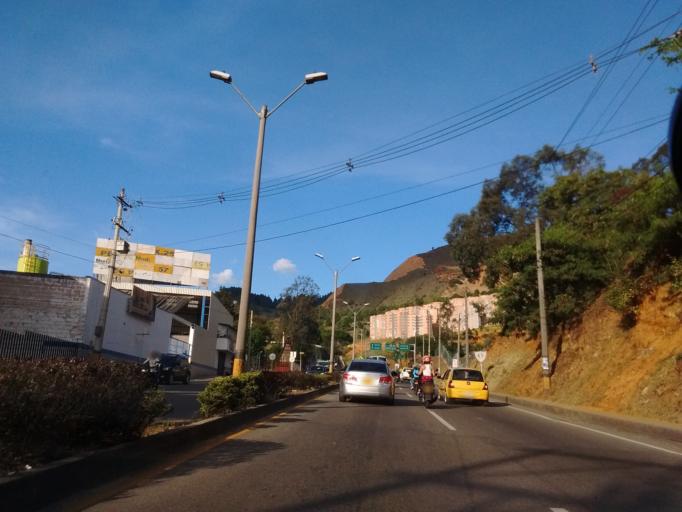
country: CO
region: Antioquia
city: Bello
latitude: 6.3102
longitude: -75.5534
